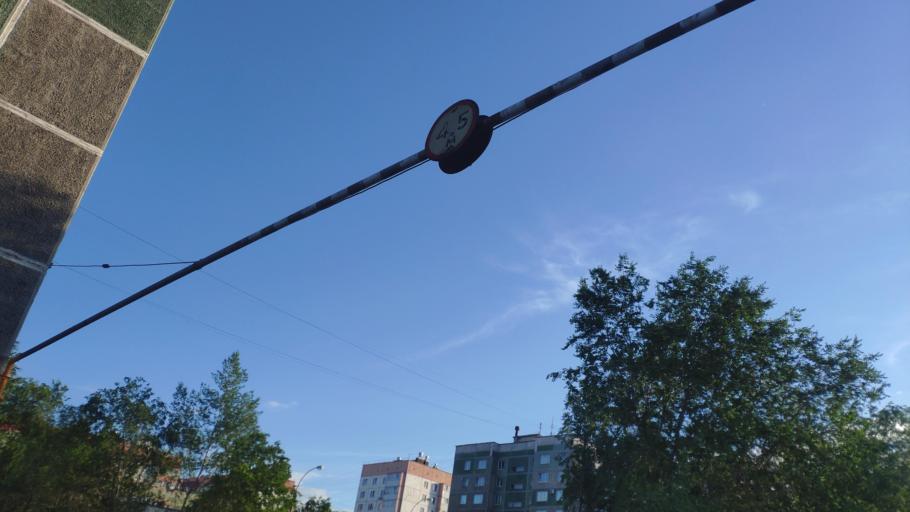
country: RU
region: Chelyabinsk
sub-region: Gorod Magnitogorsk
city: Magnitogorsk
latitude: 53.4081
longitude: 58.9653
